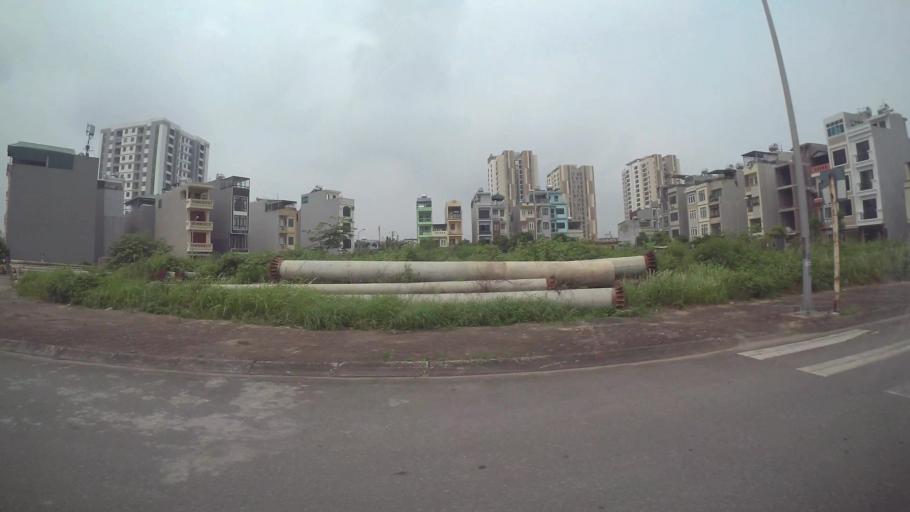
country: VN
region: Ha Noi
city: Trau Quy
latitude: 21.0640
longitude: 105.9143
